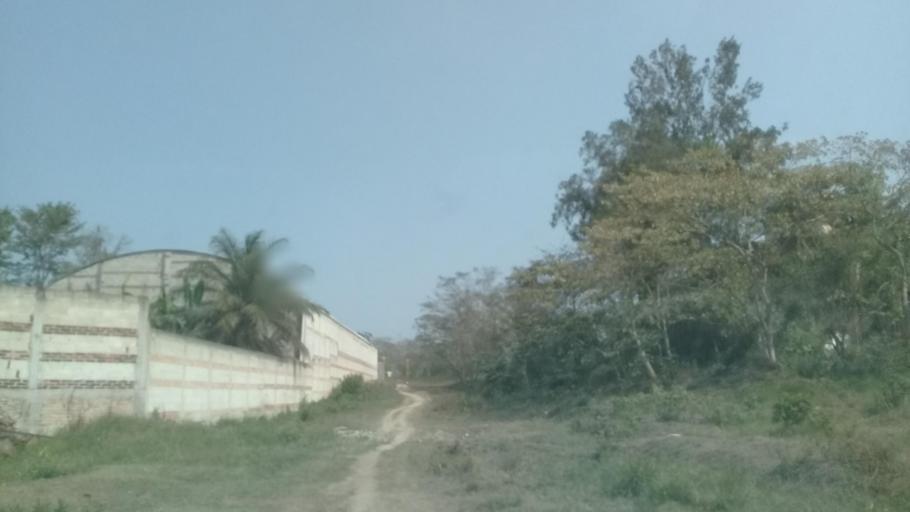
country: MX
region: Veracruz
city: El Castillo
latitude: 19.5449
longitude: -96.8523
